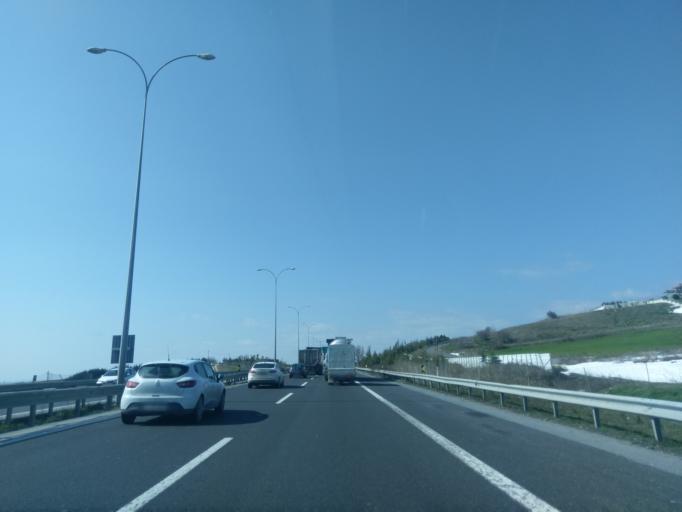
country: TR
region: Istanbul
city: Celaliye
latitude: 41.0672
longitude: 28.3935
